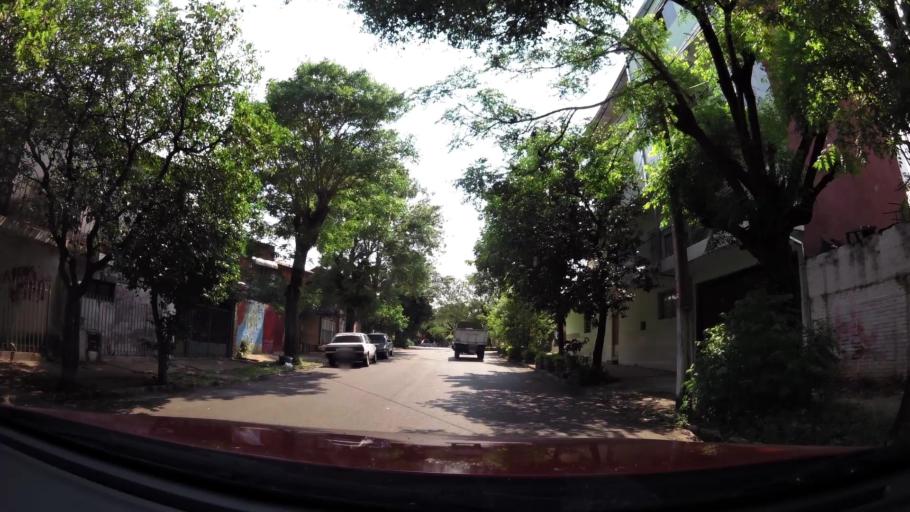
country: PY
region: Asuncion
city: Asuncion
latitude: -25.2921
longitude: -57.6541
